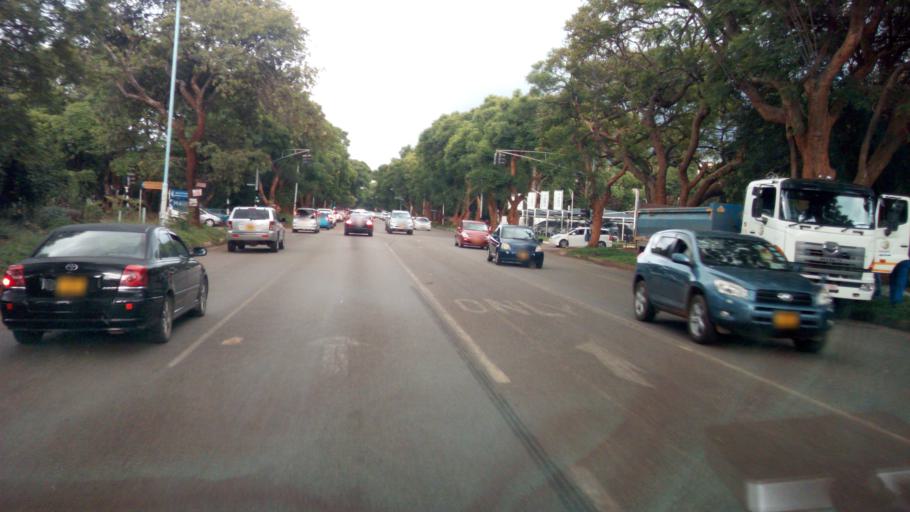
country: ZW
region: Harare
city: Harare
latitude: -17.8165
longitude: 31.0454
